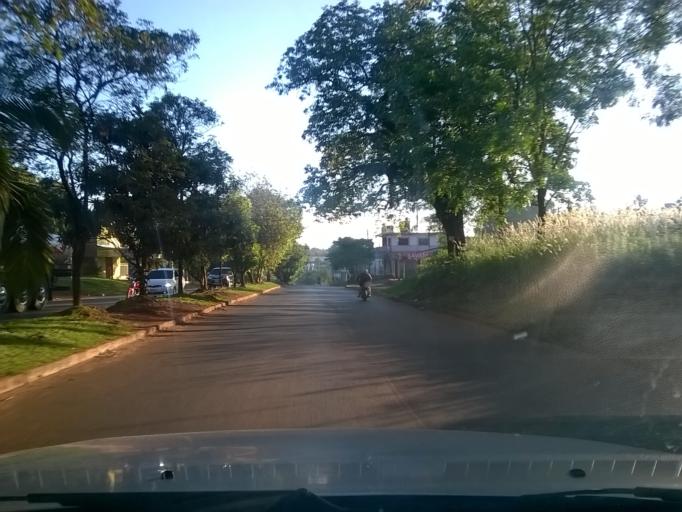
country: PY
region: Alto Parana
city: Presidente Franco
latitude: -25.5277
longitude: -54.6470
